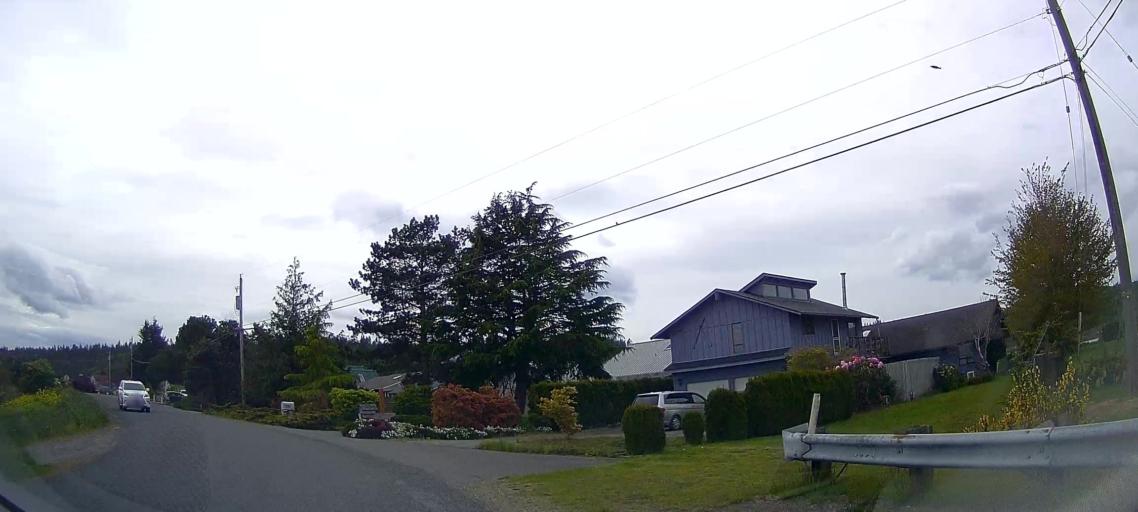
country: US
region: Washington
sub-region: Skagit County
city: Anacortes
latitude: 48.4271
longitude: -122.4983
